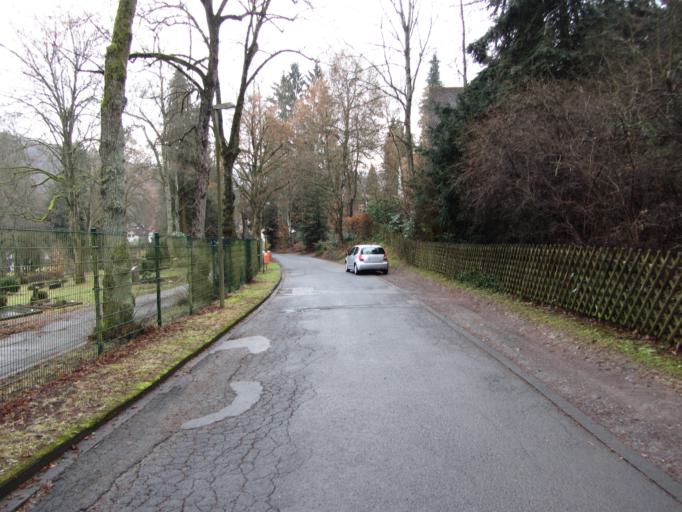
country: DE
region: North Rhine-Westphalia
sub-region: Regierungsbezirk Arnsberg
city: Siegen
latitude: 50.8871
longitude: 8.0068
